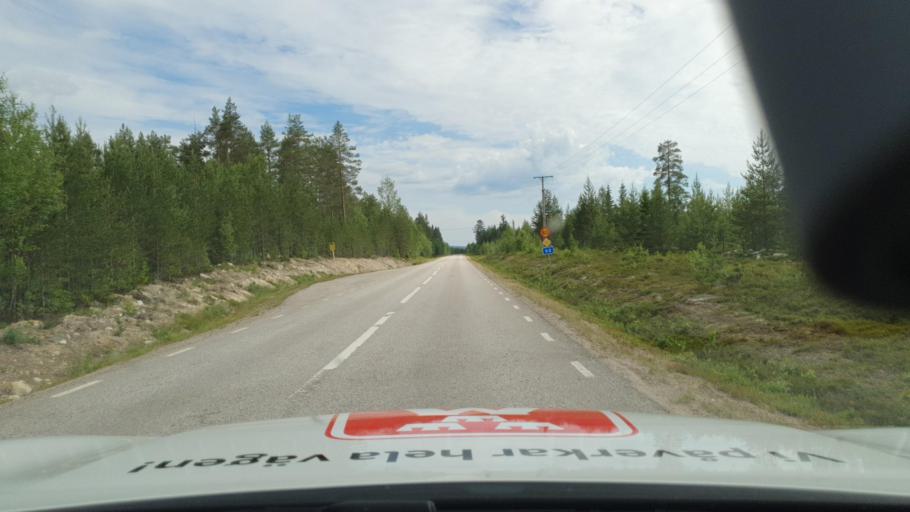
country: NO
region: Hedmark
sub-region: Trysil
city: Innbygda
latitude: 60.9835
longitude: 12.4926
